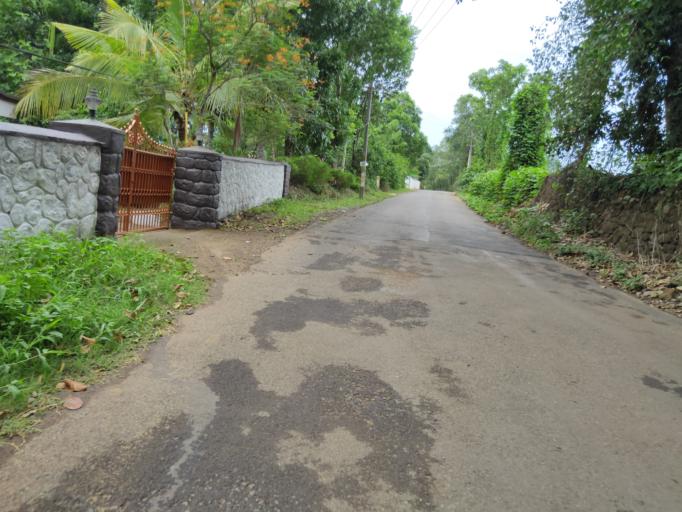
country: IN
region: Kerala
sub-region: Malappuram
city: Manjeri
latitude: 11.2381
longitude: 76.2459
